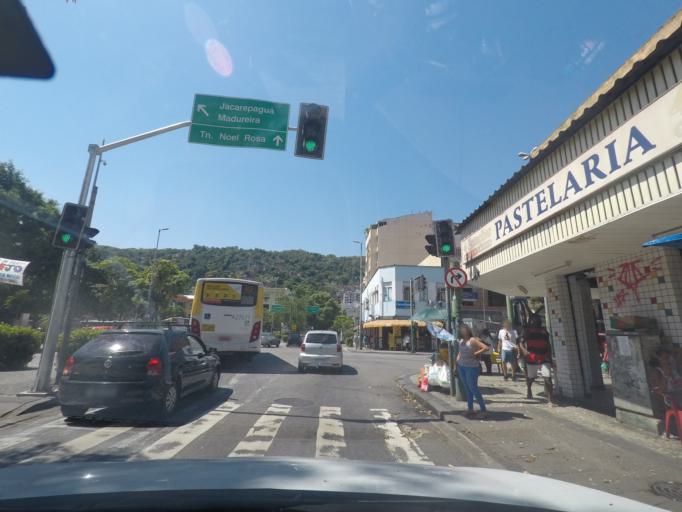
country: BR
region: Rio de Janeiro
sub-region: Rio De Janeiro
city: Rio de Janeiro
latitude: -22.9168
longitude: -43.2501
